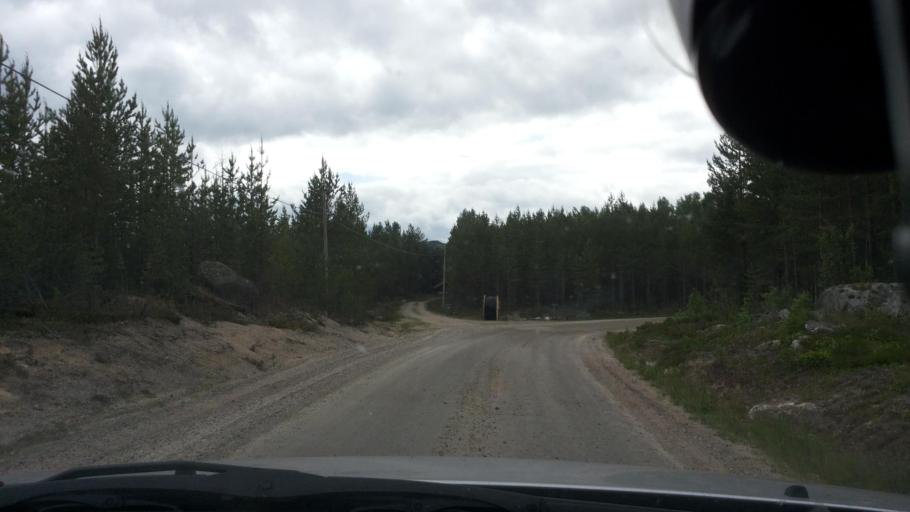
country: SE
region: Gaevleborg
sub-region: Ovanakers Kommun
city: Edsbyn
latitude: 61.5158
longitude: 15.3543
